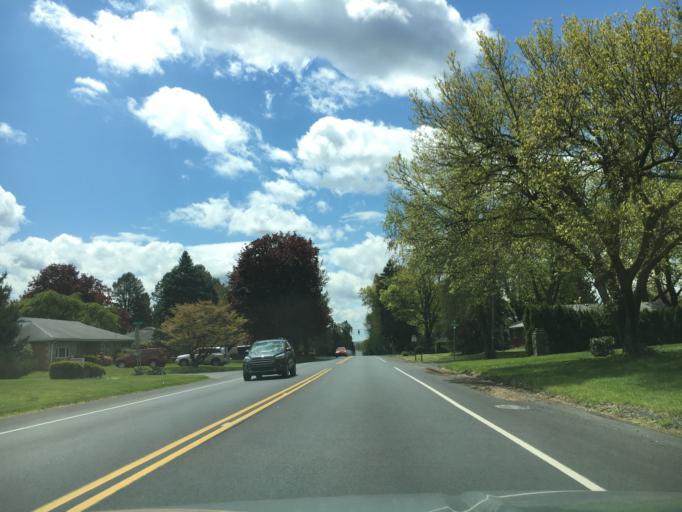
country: US
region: Pennsylvania
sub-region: Lehigh County
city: Dorneyville
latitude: 40.6072
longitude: -75.5308
